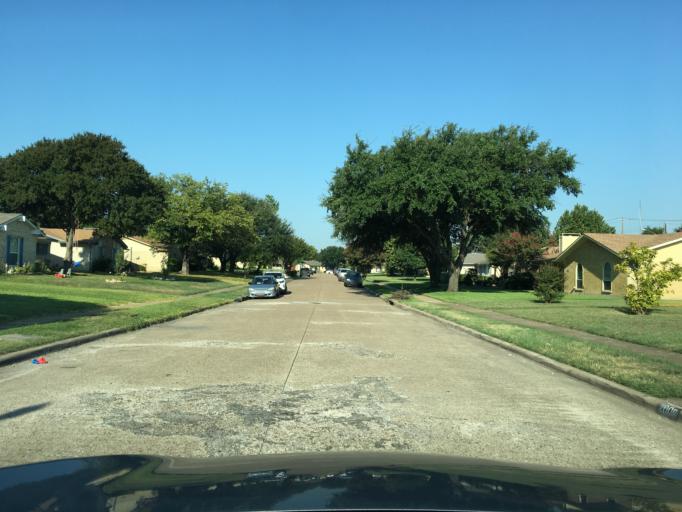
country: US
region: Texas
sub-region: Dallas County
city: Garland
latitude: 32.9509
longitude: -96.6582
